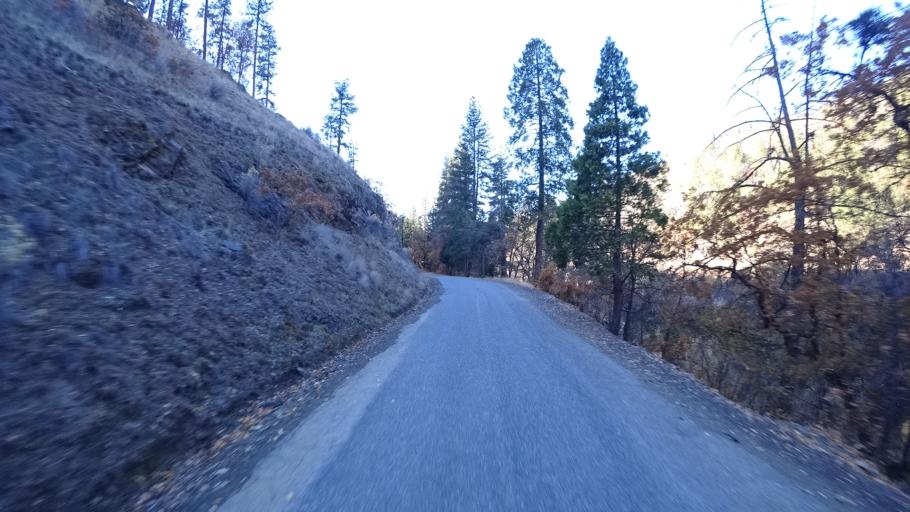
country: US
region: California
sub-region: Siskiyou County
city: Yreka
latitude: 41.8336
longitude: -122.9462
